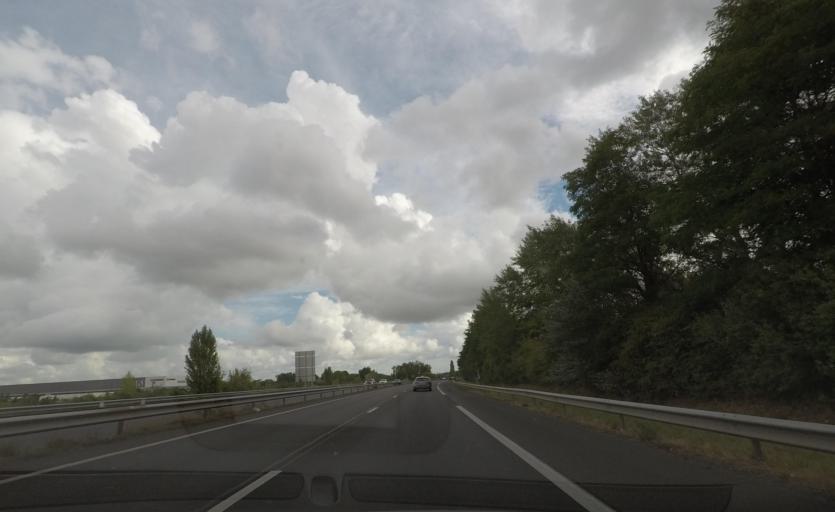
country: FR
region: Pays de la Loire
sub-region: Departement de Maine-et-Loire
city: Pellouailles-les-Vignes
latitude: 47.5136
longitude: -0.4412
